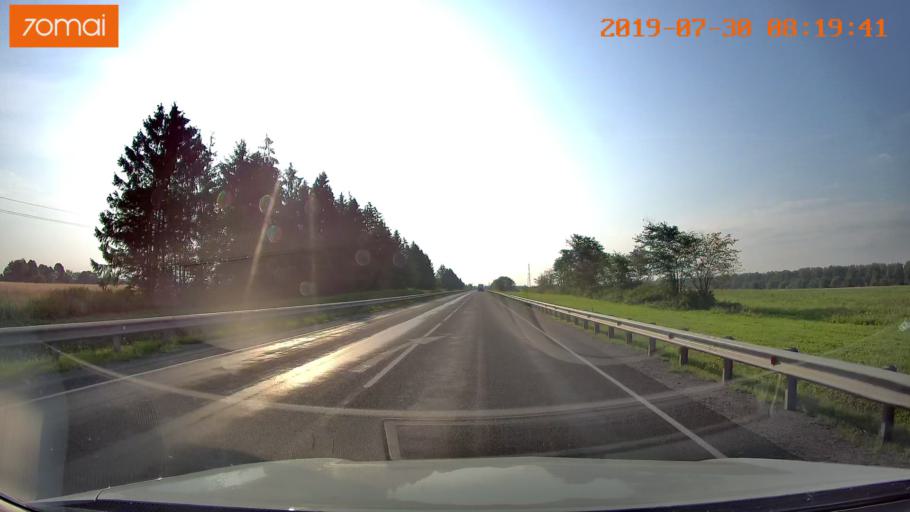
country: RU
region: Kaliningrad
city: Chernyakhovsk
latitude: 54.6275
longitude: 21.4980
